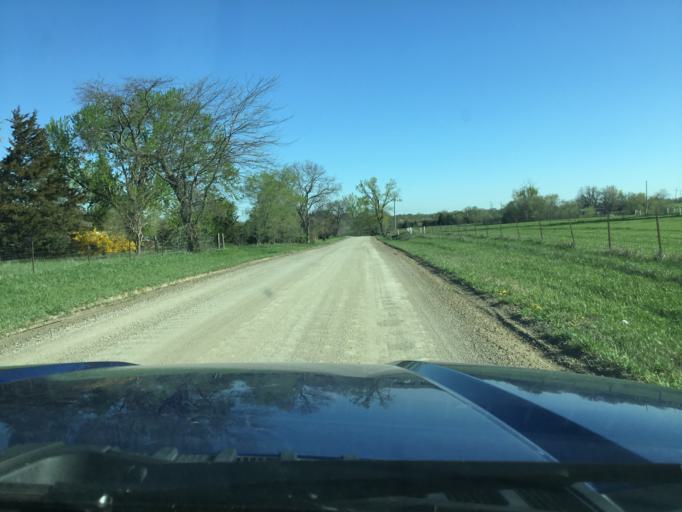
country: US
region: Kansas
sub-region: Douglas County
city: Lawrence
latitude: 38.9678
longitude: -95.3725
